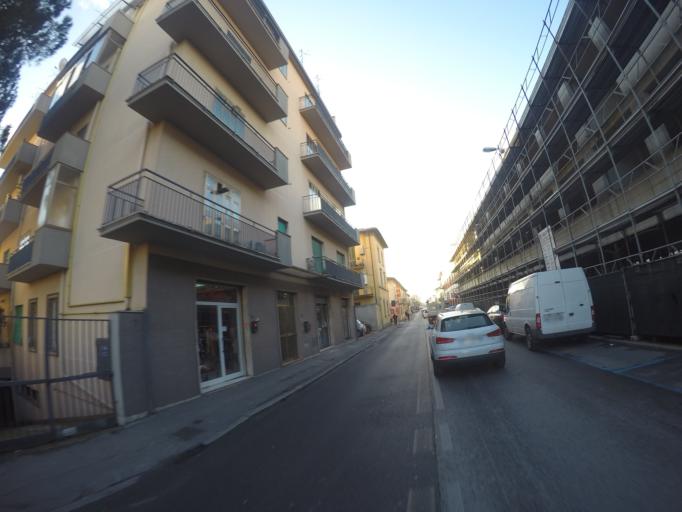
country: IT
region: Tuscany
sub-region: Provincia di Prato
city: Prato
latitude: 43.8851
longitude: 11.0901
